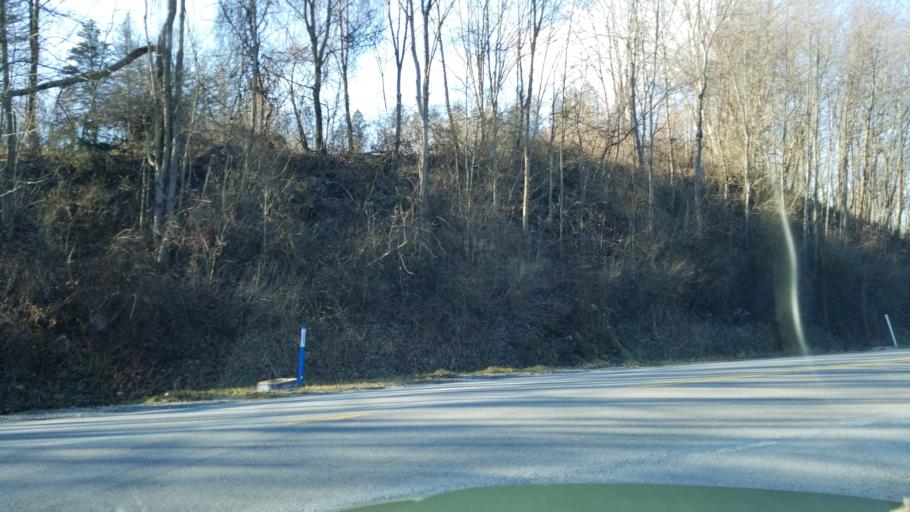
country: US
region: Pennsylvania
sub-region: Clearfield County
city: Clearfield
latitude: 41.0030
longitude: -78.4224
